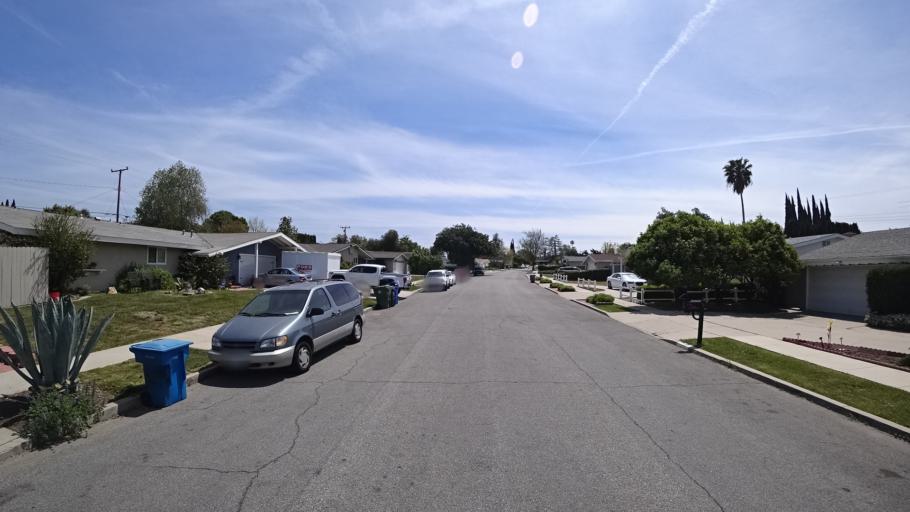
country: US
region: California
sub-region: Ventura County
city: Thousand Oaks
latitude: 34.1941
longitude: -118.8695
